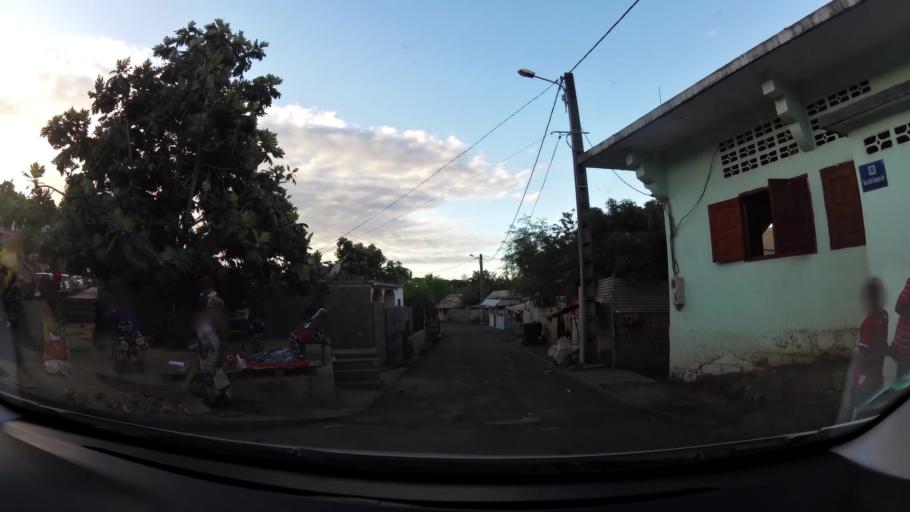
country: YT
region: Koungou
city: Koungou
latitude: -12.7332
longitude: 45.1990
